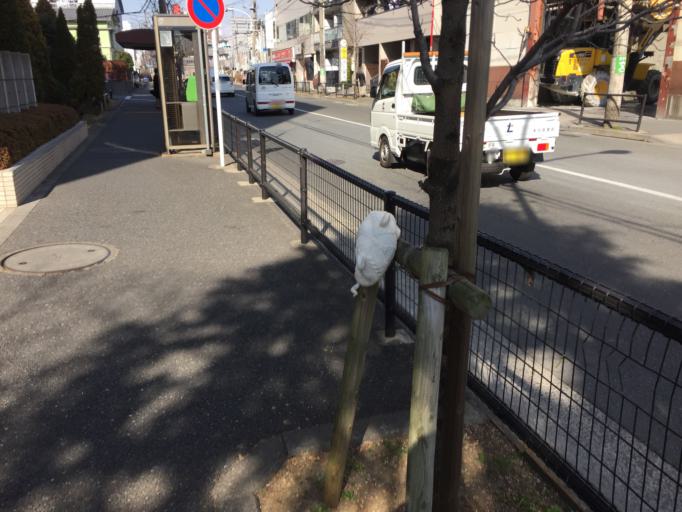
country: JP
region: Tokyo
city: Tokyo
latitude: 35.6400
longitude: 139.6822
